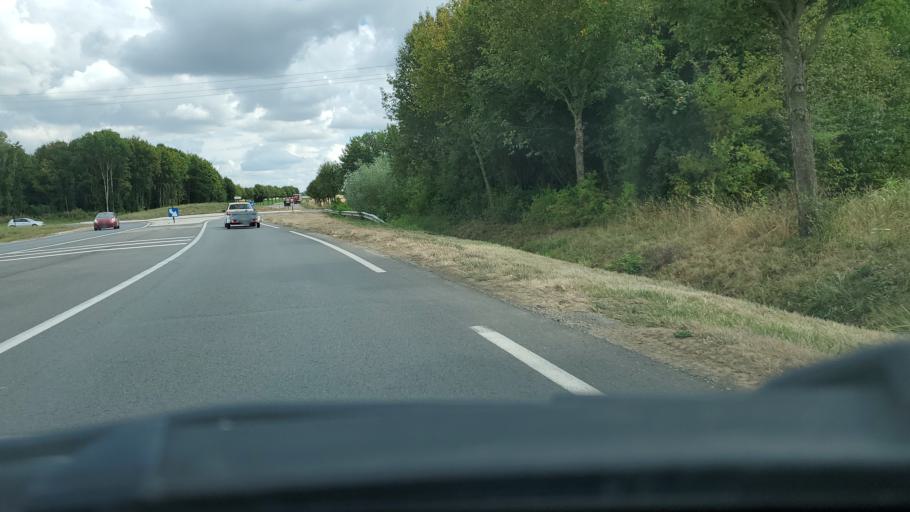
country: FR
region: Ile-de-France
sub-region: Departement de Seine-et-Marne
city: Nanteuil-les-Meaux
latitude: 48.9120
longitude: 2.9193
